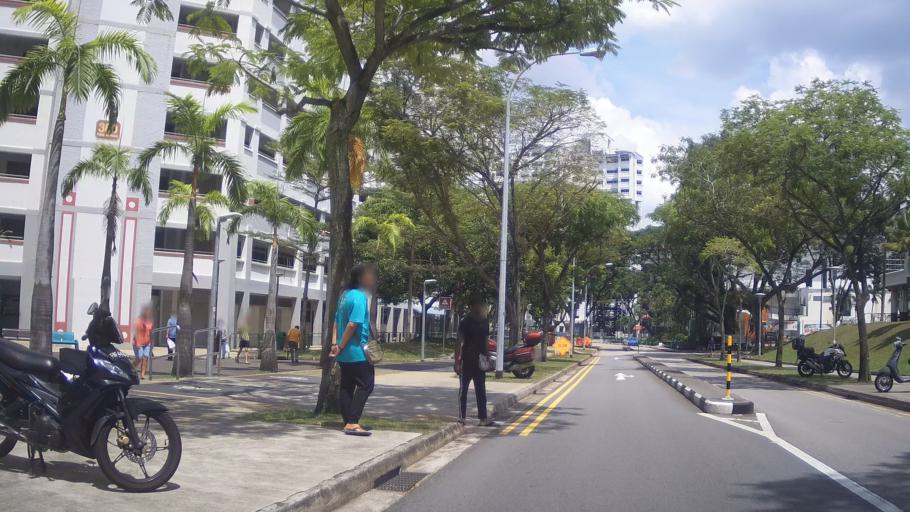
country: MY
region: Johor
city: Johor Bahru
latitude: 1.3357
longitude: 103.7206
